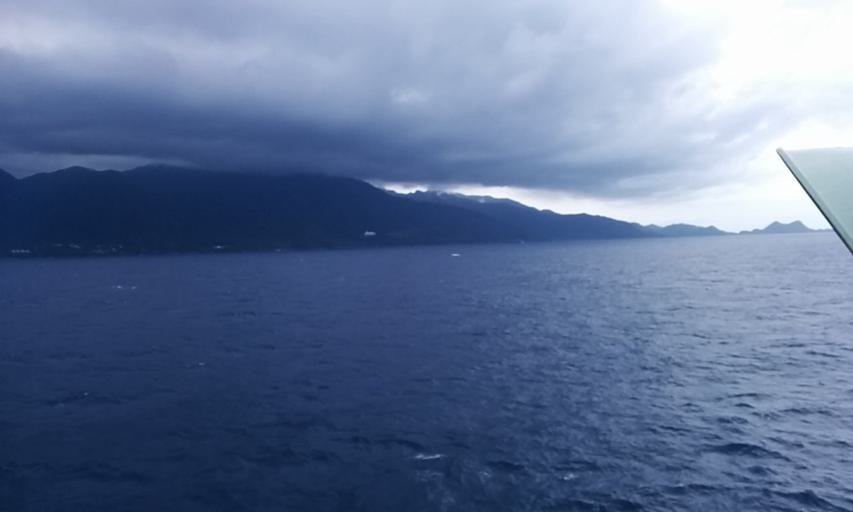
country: JP
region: Kagoshima
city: Nishinoomote
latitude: 30.4562
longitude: 130.5847
